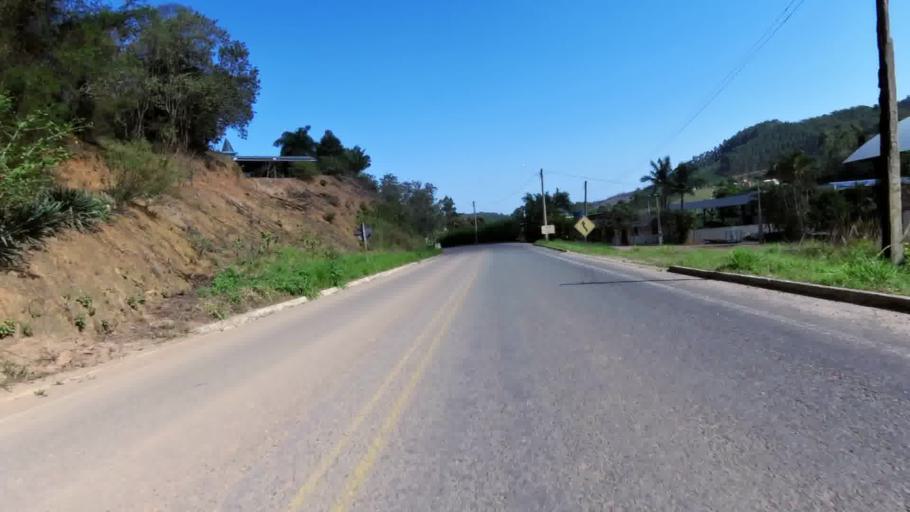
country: BR
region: Espirito Santo
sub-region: Alfredo Chaves
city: Alfredo Chaves
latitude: -20.5204
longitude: -40.7766
